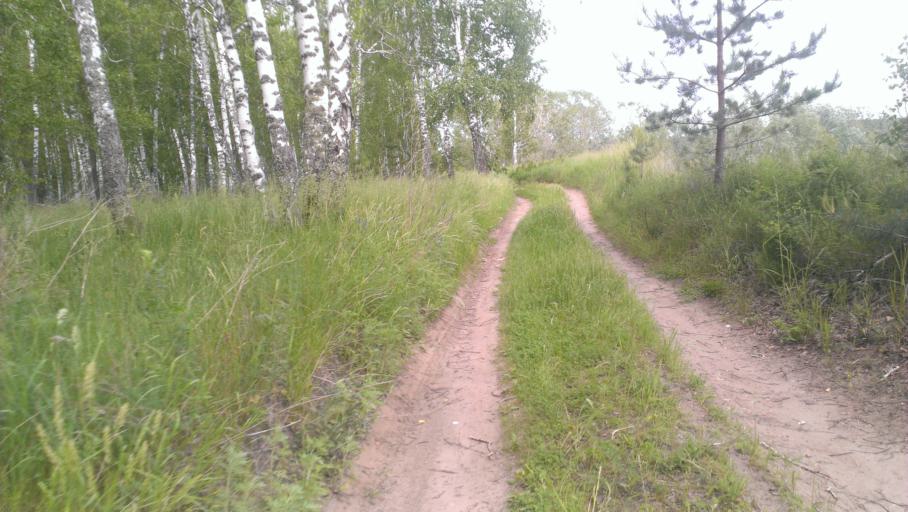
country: RU
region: Altai Krai
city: Sannikovo
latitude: 53.3387
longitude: 84.0554
